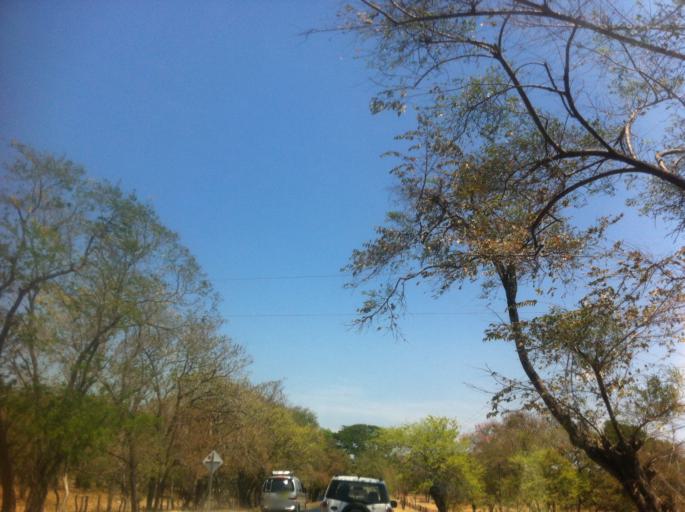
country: CR
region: Guanacaste
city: Belen
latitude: 10.3830
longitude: -85.5844
